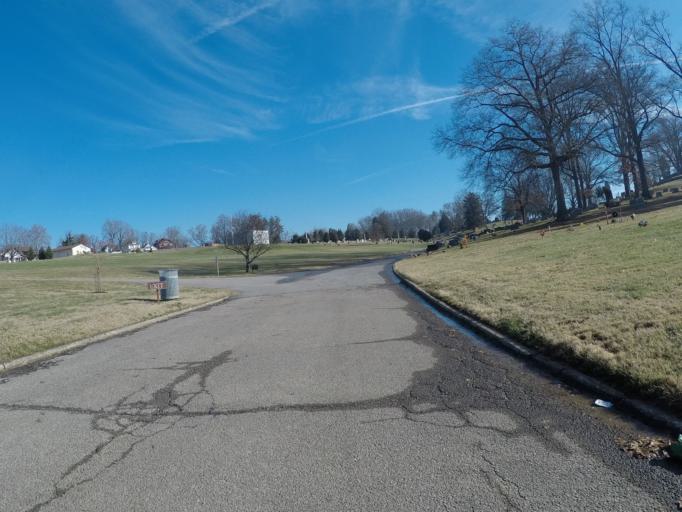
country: US
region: West Virginia
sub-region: Cabell County
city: Huntington
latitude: 38.4103
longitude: -82.4170
